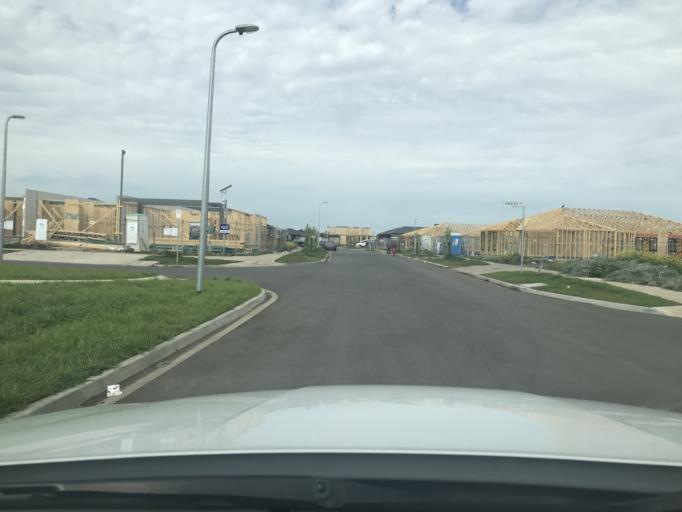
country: AU
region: Victoria
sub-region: Hume
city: Roxburgh Park
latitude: -37.6017
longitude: 144.8980
